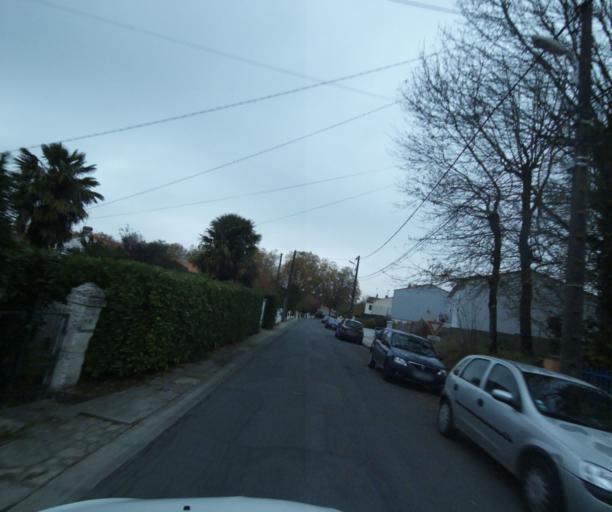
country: FR
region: Poitou-Charentes
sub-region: Departement de la Charente-Maritime
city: Saintes
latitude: 45.7434
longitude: -0.6067
